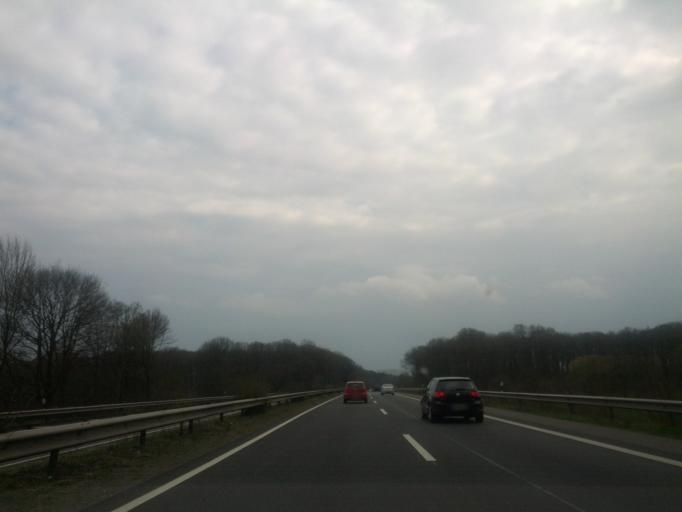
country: DE
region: Lower Saxony
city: Westerstede
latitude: 53.2775
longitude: 7.9093
